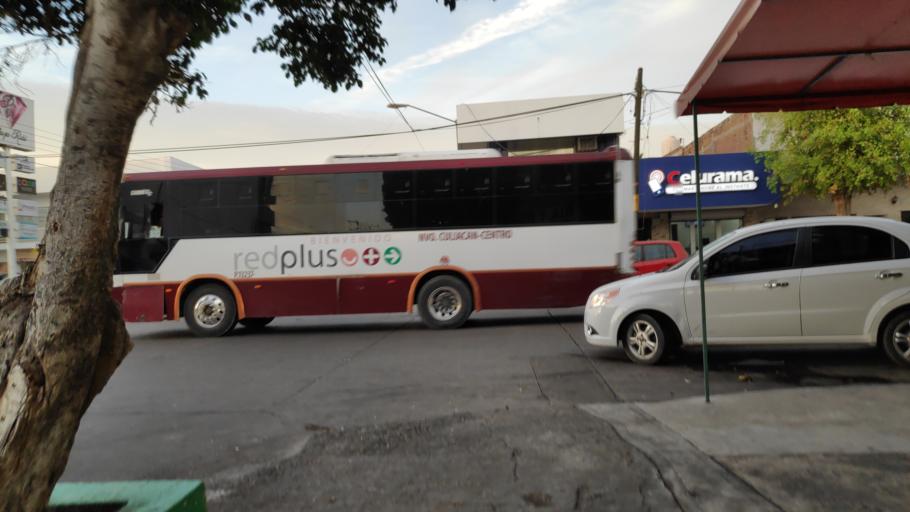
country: MX
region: Sinaloa
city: Culiacan
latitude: 24.8008
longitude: -107.3953
